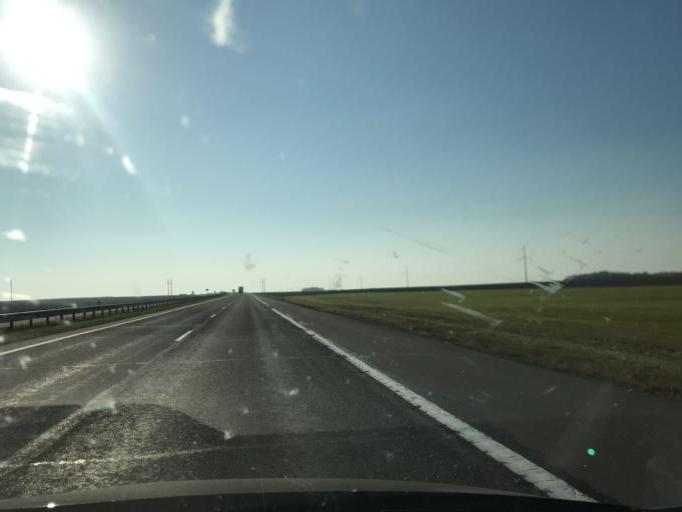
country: BY
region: Minsk
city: Snow
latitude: 53.3296
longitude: 26.4209
